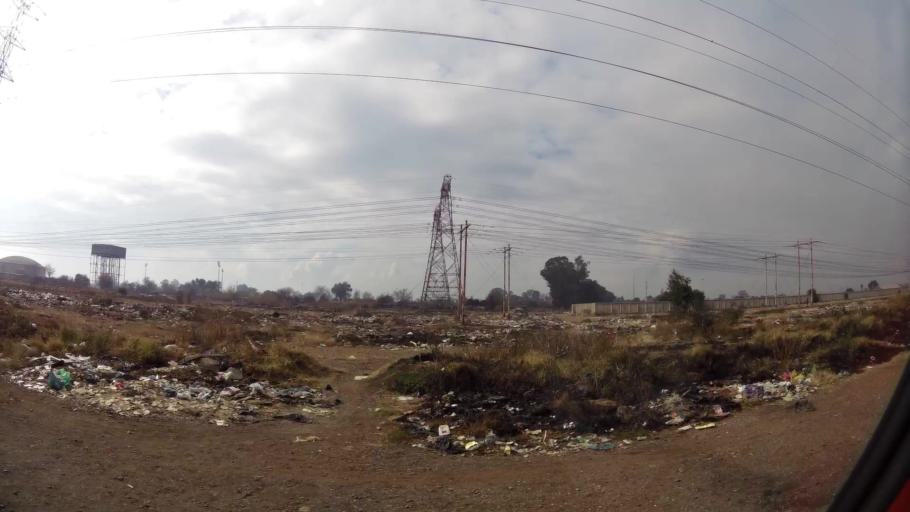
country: ZA
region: Gauteng
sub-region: Sedibeng District Municipality
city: Vanderbijlpark
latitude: -26.6905
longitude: 27.8608
